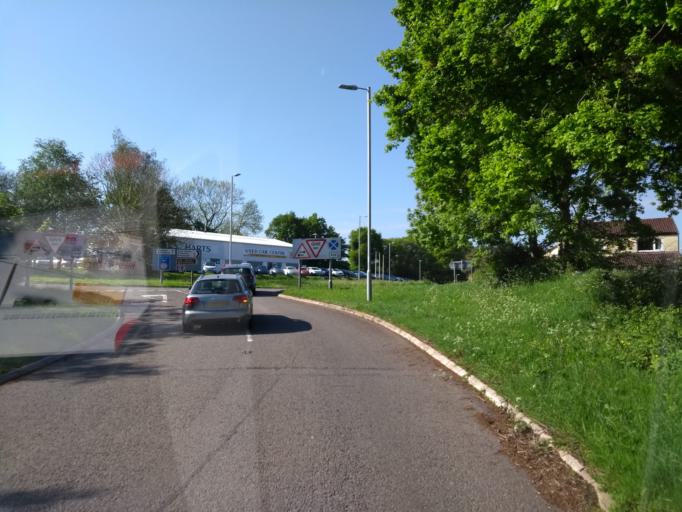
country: GB
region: England
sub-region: Devon
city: Honiton
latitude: 50.8048
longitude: -3.1758
